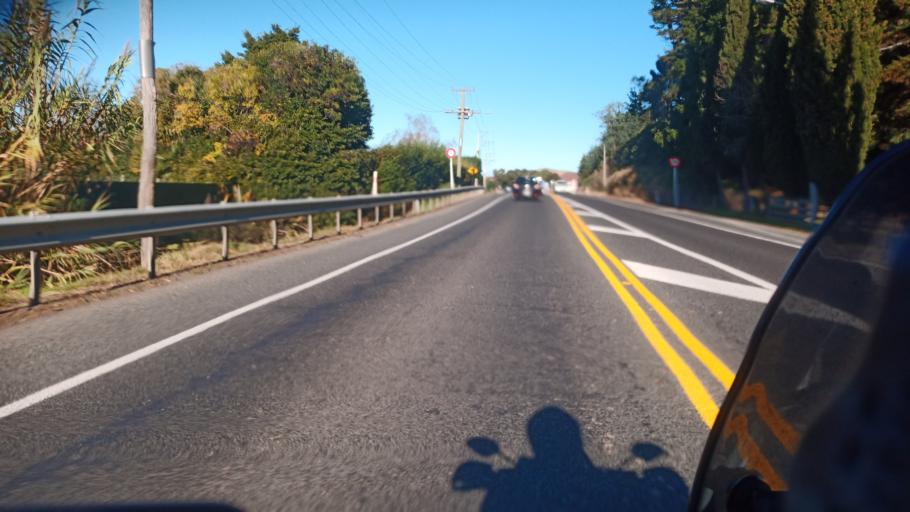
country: NZ
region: Hawke's Bay
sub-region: Napier City
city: Napier
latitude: -39.4169
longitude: 176.8688
